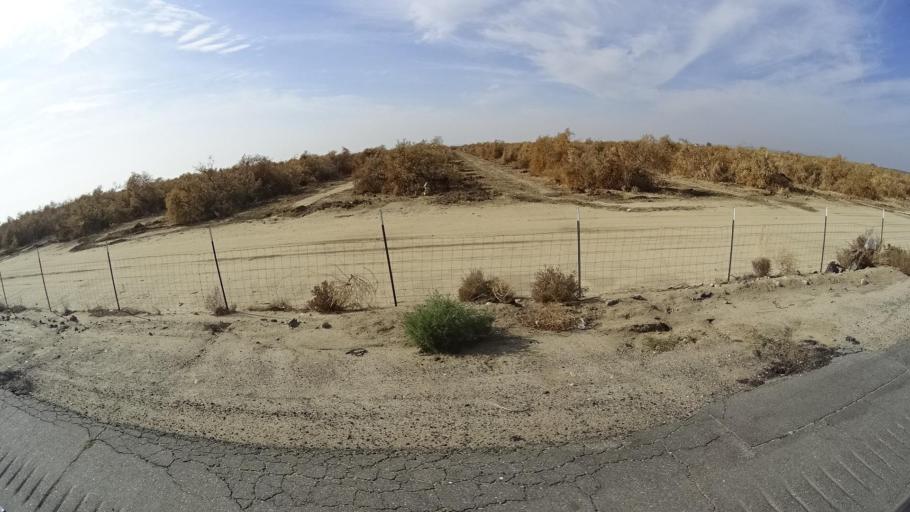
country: US
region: California
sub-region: Kern County
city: Lamont
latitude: 35.3352
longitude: -118.8432
